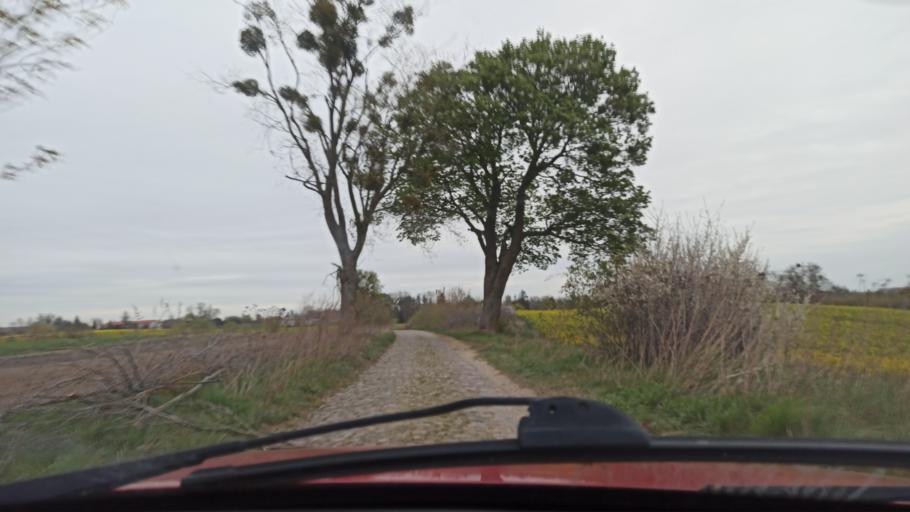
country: PL
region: Kujawsko-Pomorskie
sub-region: Powiat grudziadzki
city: Lasin
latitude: 53.5797
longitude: 19.0907
